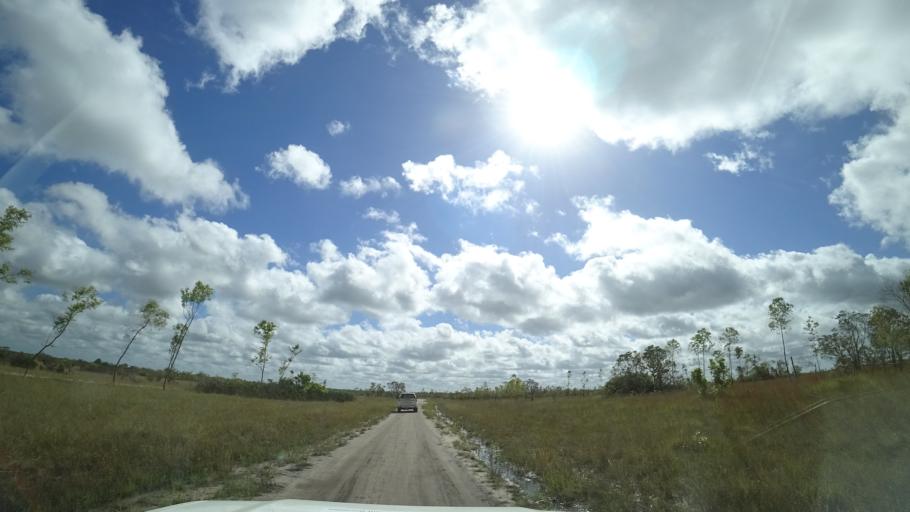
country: MZ
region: Sofala
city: Dondo
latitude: -19.6030
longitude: 35.0844
